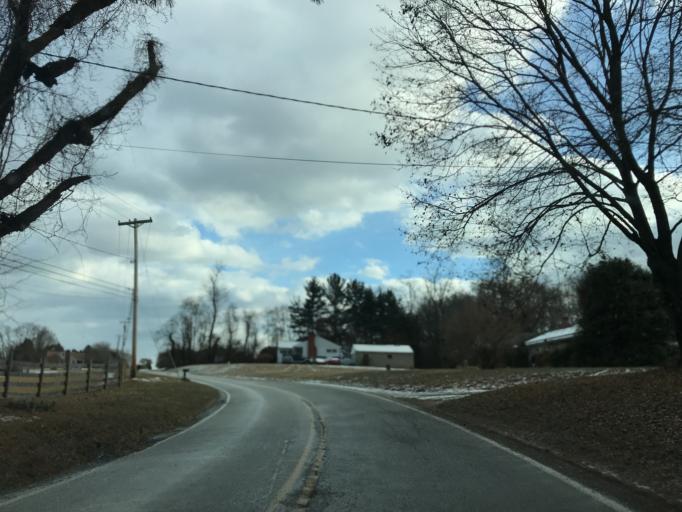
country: US
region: Maryland
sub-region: Harford County
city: Jarrettsville
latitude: 39.6158
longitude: -76.4501
